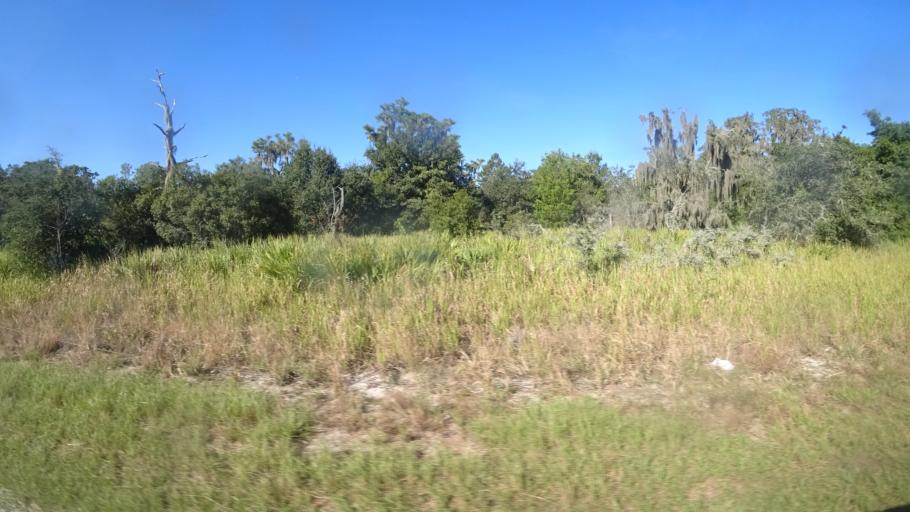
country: US
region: Florida
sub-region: Hillsborough County
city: Wimauma
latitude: 27.6399
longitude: -82.2924
